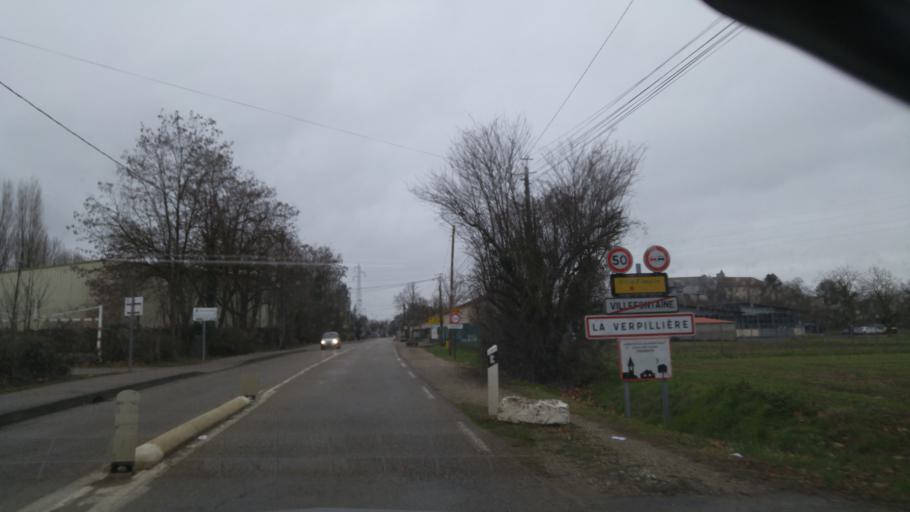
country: FR
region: Rhone-Alpes
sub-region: Departement de l'Isere
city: Villefontaine
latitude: 45.6248
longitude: 5.1538
